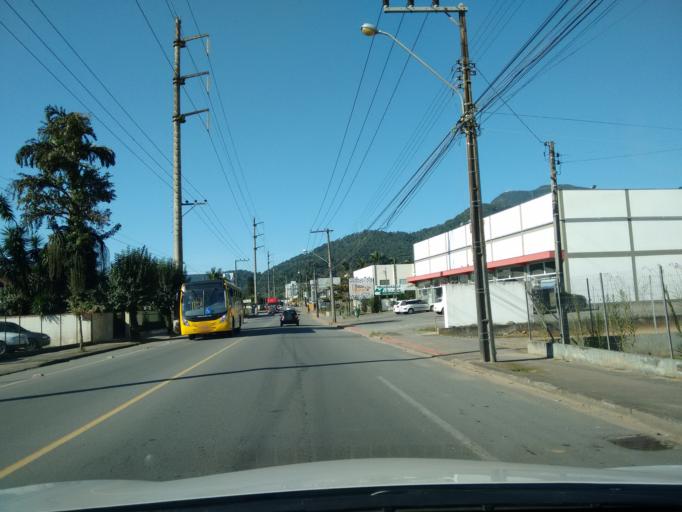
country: BR
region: Santa Catarina
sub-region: Jaragua Do Sul
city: Jaragua do Sul
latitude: -26.5067
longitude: -49.0970
